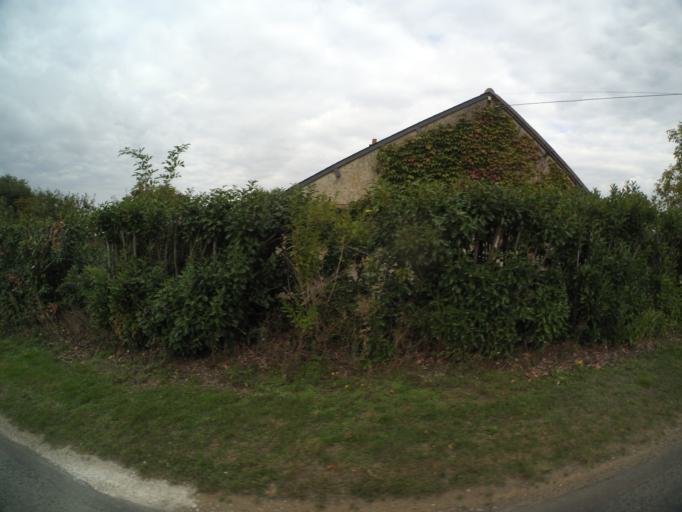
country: FR
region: Centre
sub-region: Departement d'Indre-et-Loire
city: Poce-sur-Cisse
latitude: 47.4964
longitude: 0.9824
